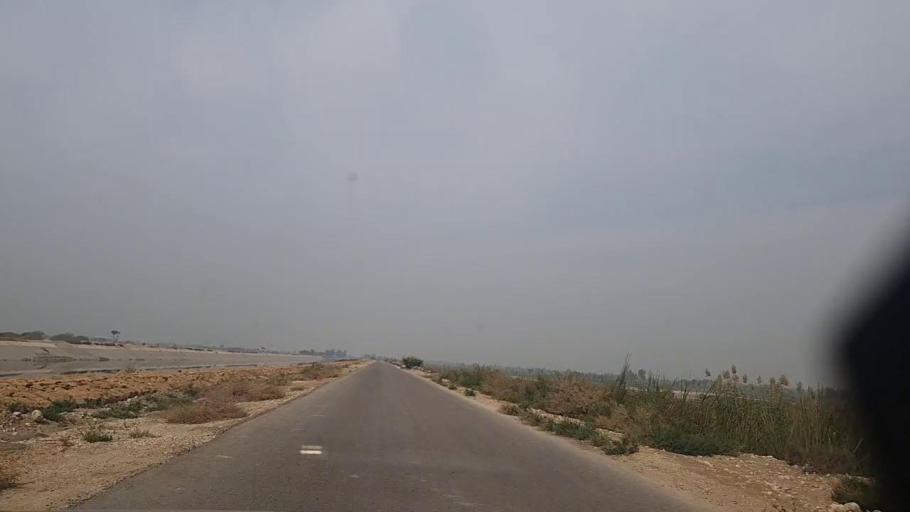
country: PK
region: Sindh
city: Sakrand
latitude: 26.2722
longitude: 68.2341
